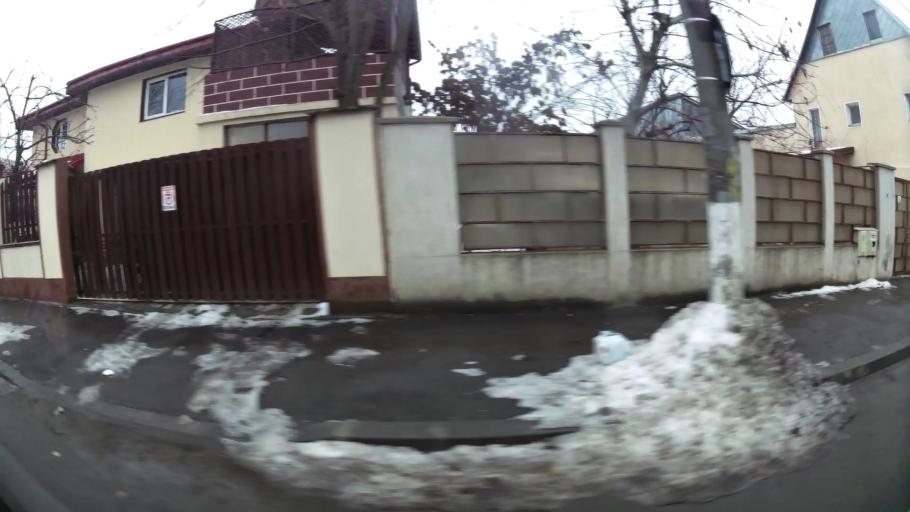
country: RO
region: Ilfov
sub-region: Comuna Chiajna
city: Rosu
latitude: 44.4411
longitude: 26.0098
